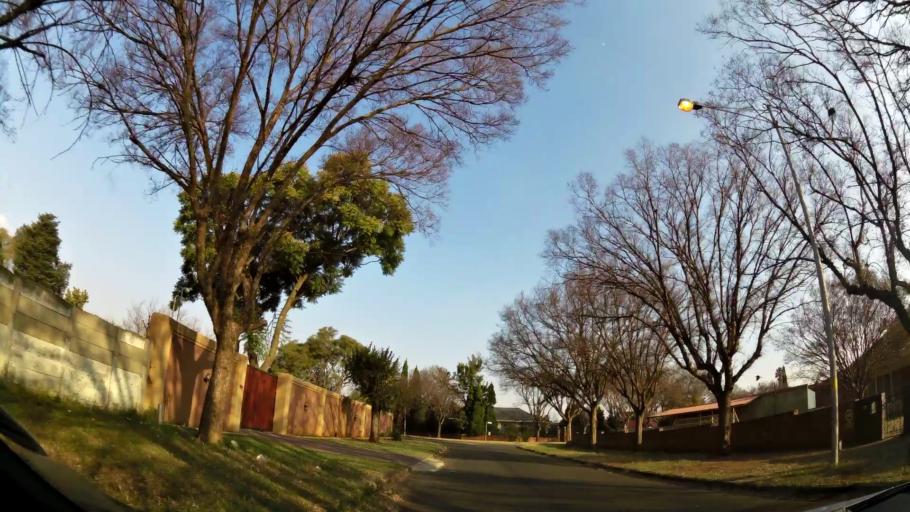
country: ZA
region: Gauteng
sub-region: Ekurhuleni Metropolitan Municipality
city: Springs
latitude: -26.2946
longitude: 28.4480
